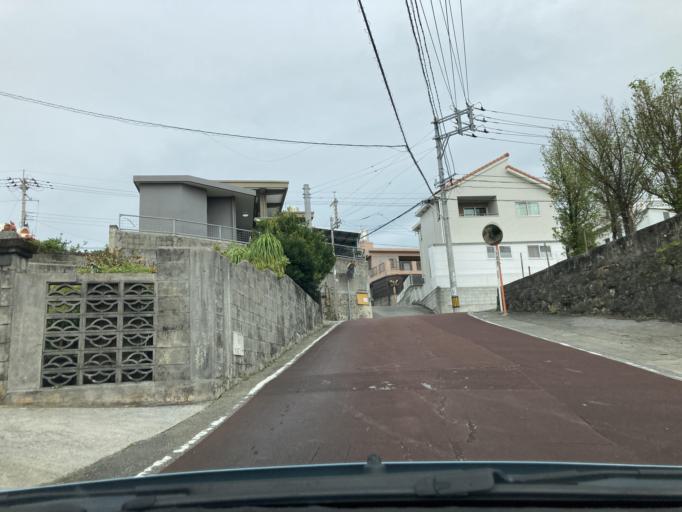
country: JP
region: Okinawa
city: Itoman
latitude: 26.1444
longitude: 127.6768
